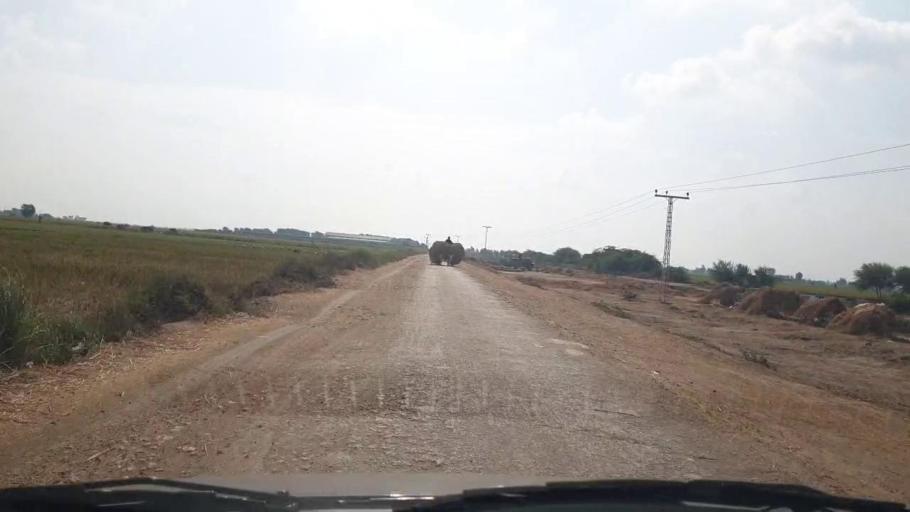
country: PK
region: Sindh
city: Kario
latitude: 24.6417
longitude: 68.5451
